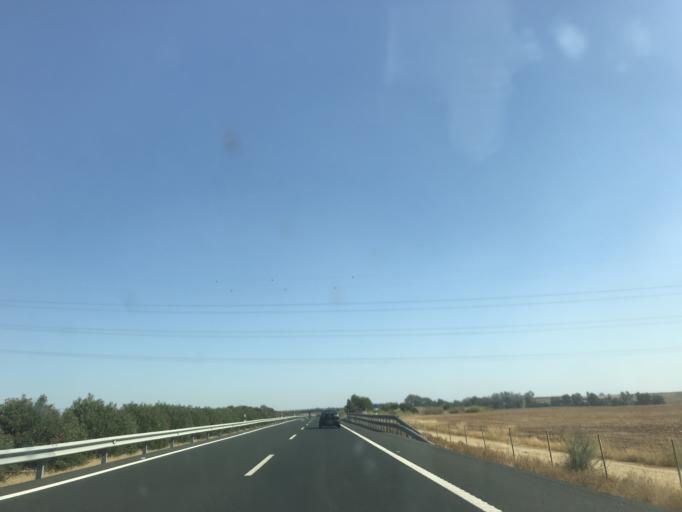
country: ES
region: Andalusia
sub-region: Provincia de Sevilla
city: Mairena del Alcor
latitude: 37.3150
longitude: -5.7565
